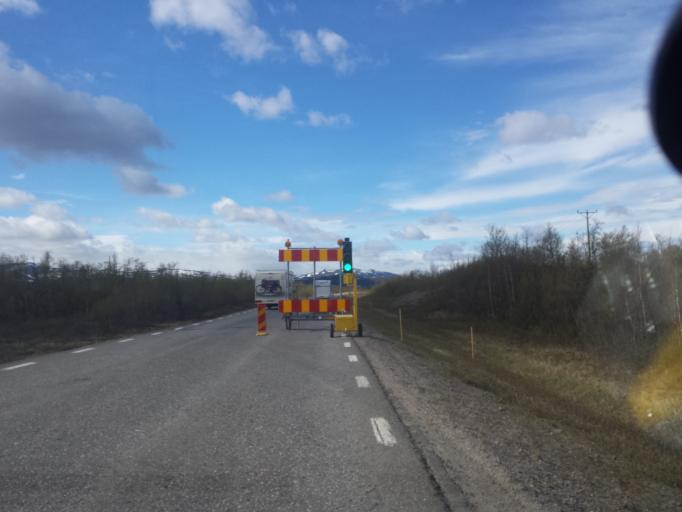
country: SE
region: Norrbotten
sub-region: Kiruna Kommun
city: Kiruna
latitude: 68.0053
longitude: 19.8518
